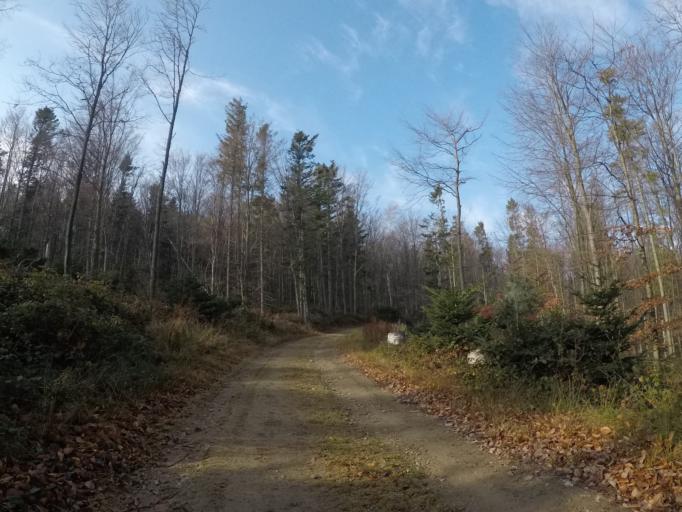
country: SK
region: Kosicky
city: Moldava nad Bodvou
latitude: 48.7635
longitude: 21.0858
